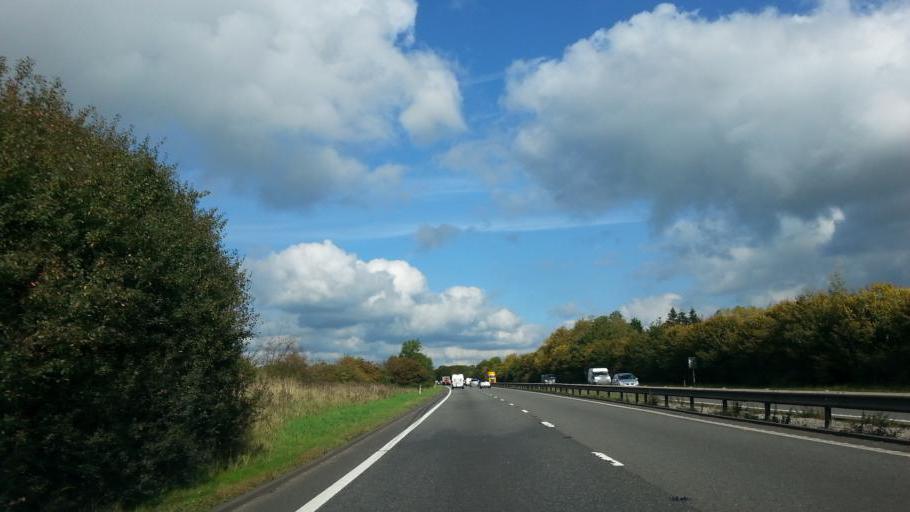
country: GB
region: England
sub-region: Derbyshire
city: Heage
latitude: 53.0386
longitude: -1.4335
